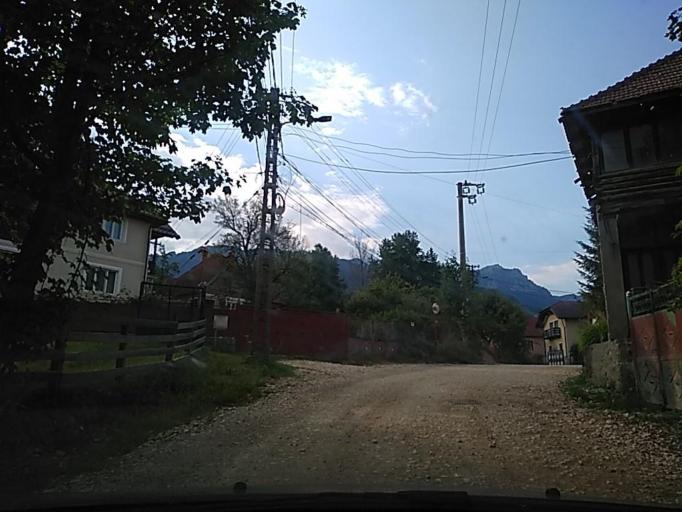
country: RO
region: Brasov
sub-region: Comuna Bran
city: Simon
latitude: 45.5019
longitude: 25.3833
